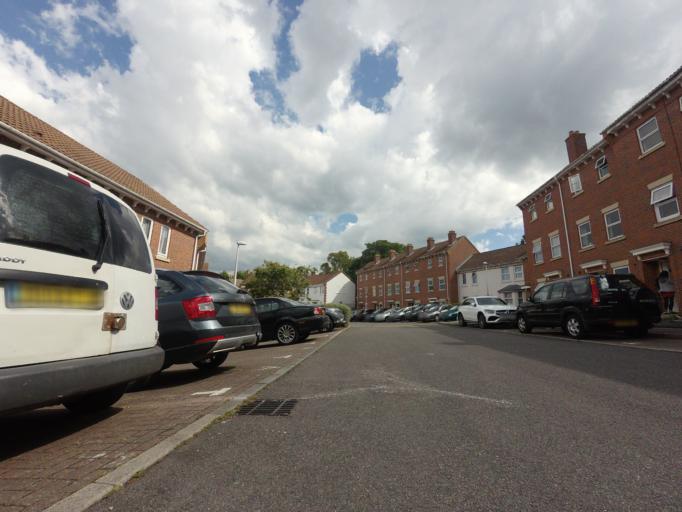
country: GB
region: England
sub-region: Kent
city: Chatham
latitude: 51.3737
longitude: 0.5321
